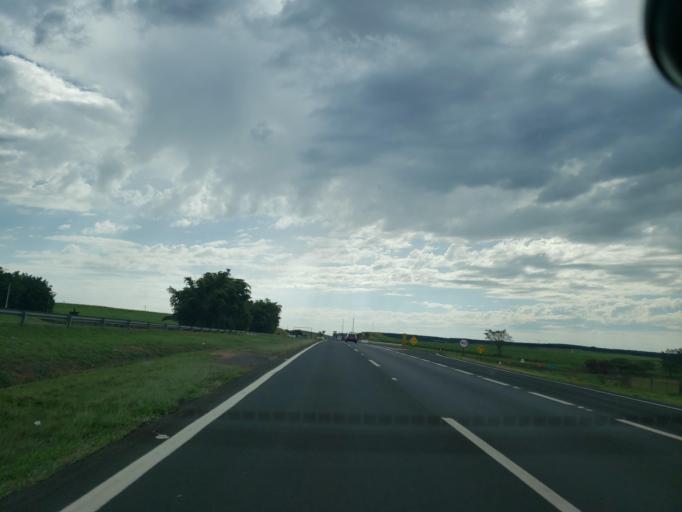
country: BR
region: Sao Paulo
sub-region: Cafelandia
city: Cafelandia
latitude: -21.7752
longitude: -49.6629
